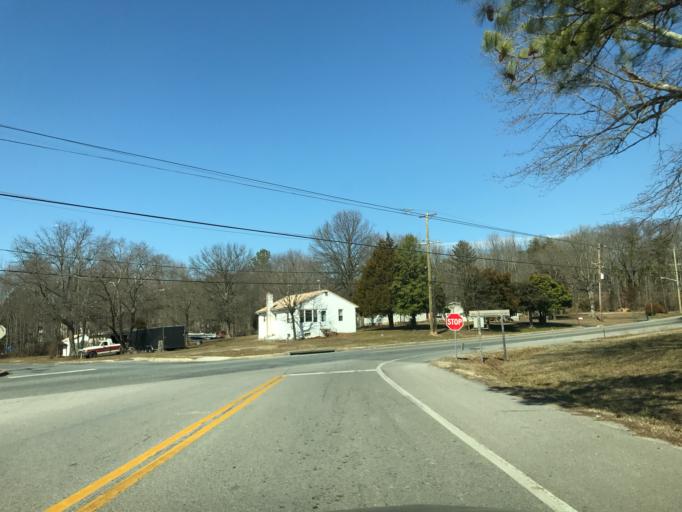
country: US
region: Maryland
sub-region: Cecil County
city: Charlestown
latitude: 39.5831
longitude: -75.9715
